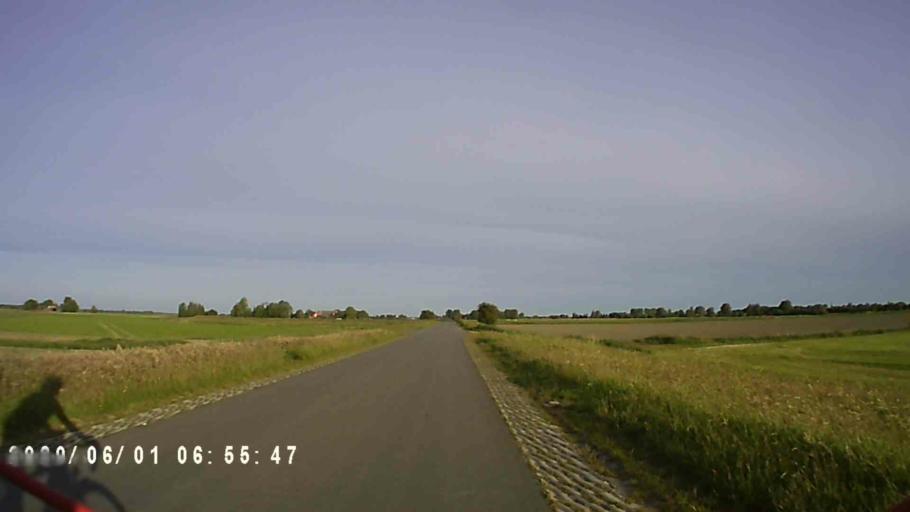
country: NL
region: Friesland
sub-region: Gemeente Kollumerland en Nieuwkruisland
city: Kollum
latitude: 53.3167
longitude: 6.1168
